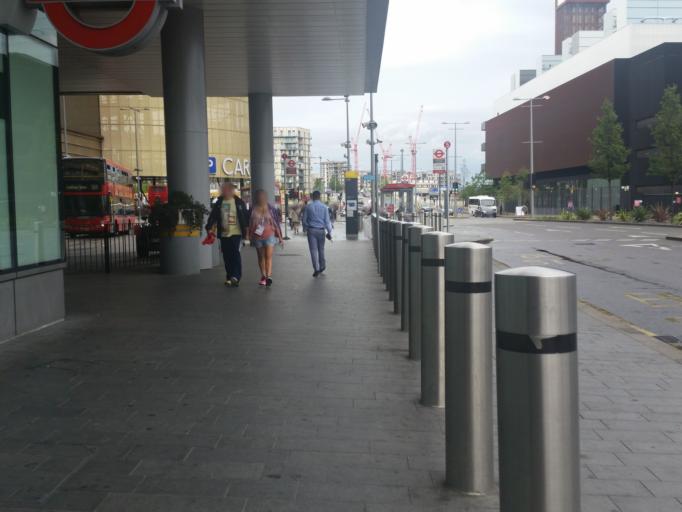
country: GB
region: England
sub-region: Greater London
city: Poplar
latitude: 51.5431
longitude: -0.0040
